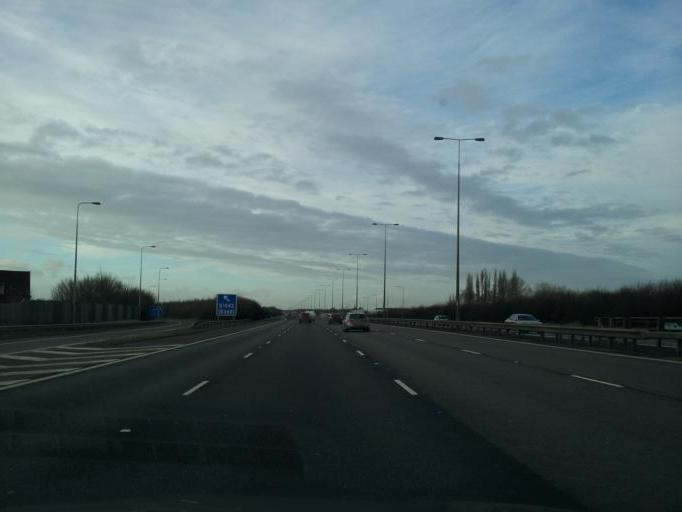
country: GB
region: England
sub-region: Cambridgeshire
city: Sawtry
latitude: 52.4268
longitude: -0.2695
